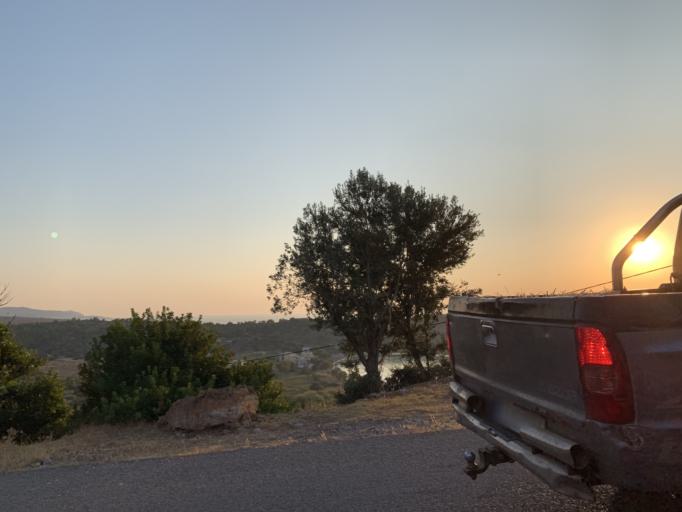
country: GR
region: North Aegean
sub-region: Chios
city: Thymiana
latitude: 38.3417
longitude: 25.9991
